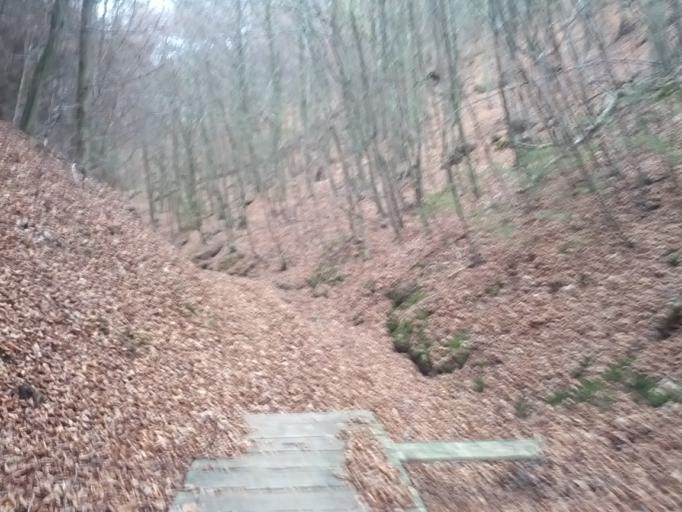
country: DE
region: Thuringia
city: Eisenach
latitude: 50.9493
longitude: 10.3273
